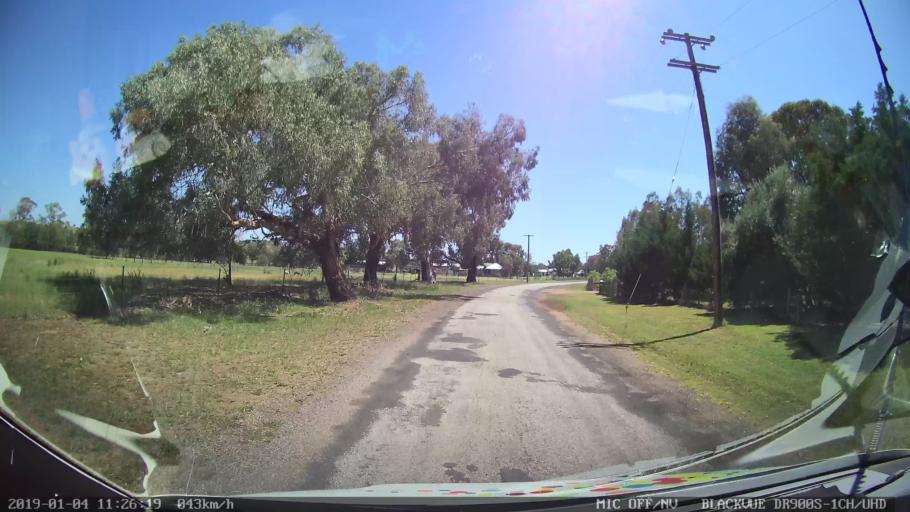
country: AU
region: New South Wales
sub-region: Cabonne
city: Molong
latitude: -33.1161
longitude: 148.7557
